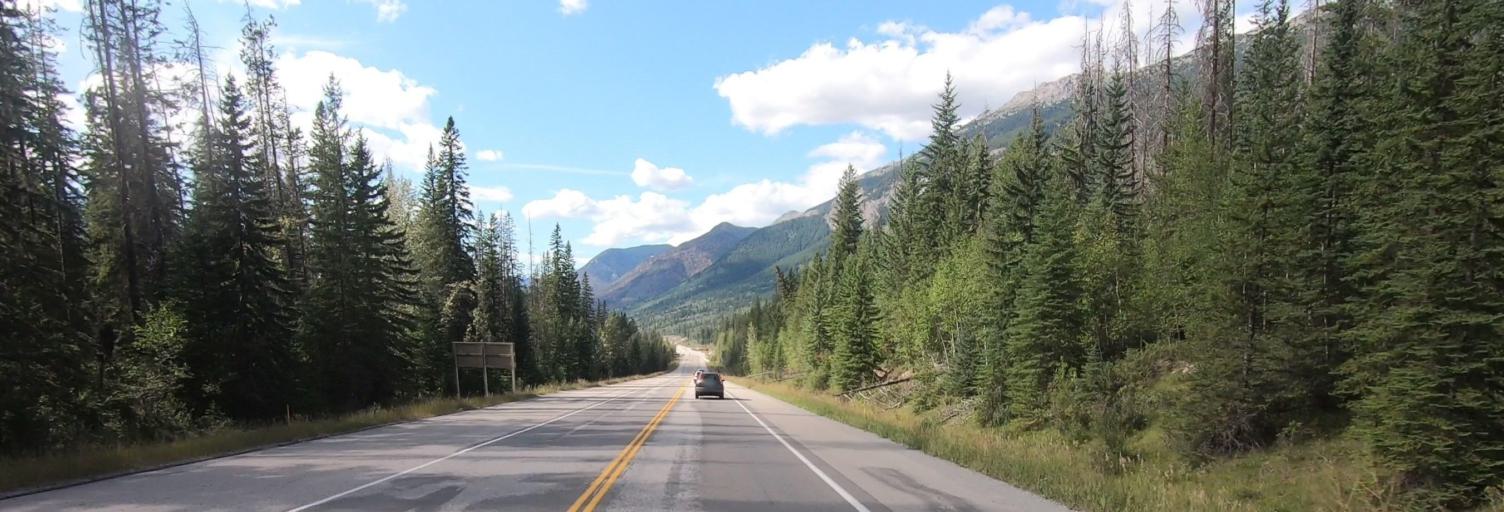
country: CA
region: British Columbia
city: Golden
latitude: 51.2343
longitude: -116.6447
